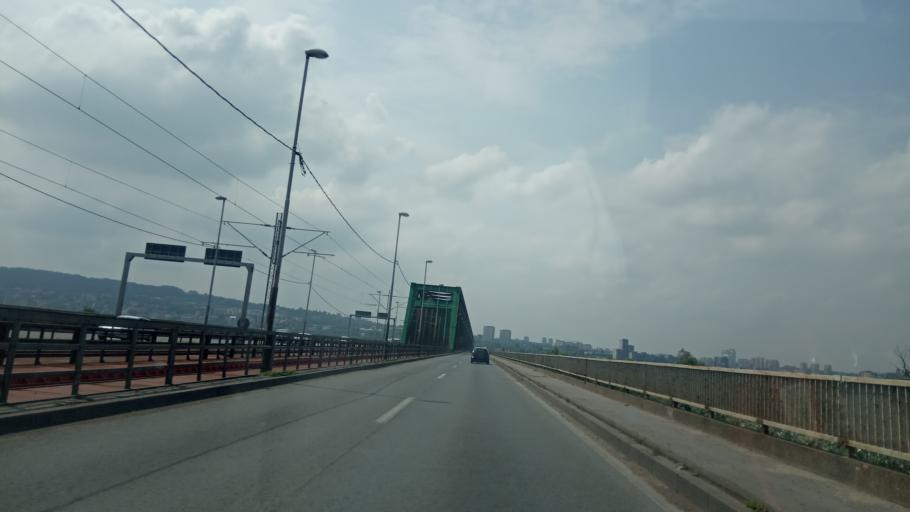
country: RS
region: Central Serbia
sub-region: Belgrade
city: Palilula
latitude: 44.8335
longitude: 20.4928
